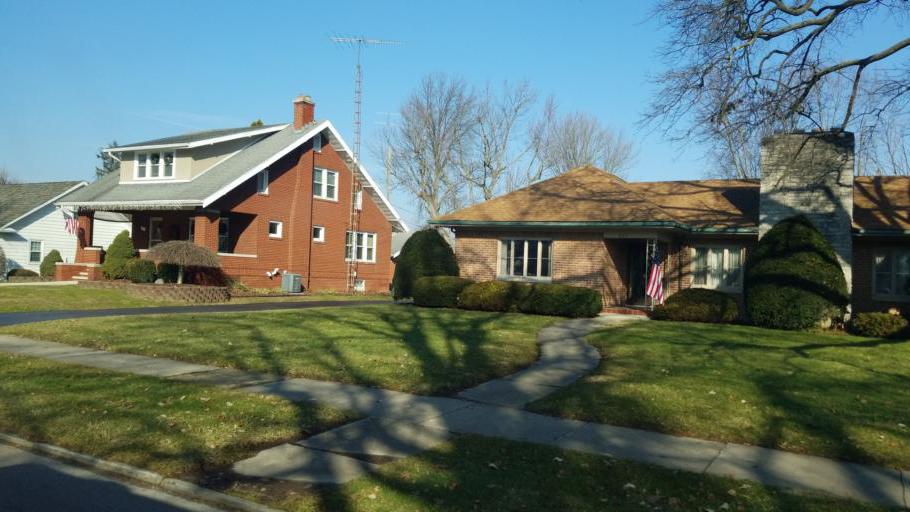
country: US
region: Ohio
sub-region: Seneca County
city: Tiffin
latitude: 41.1042
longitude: -83.1637
